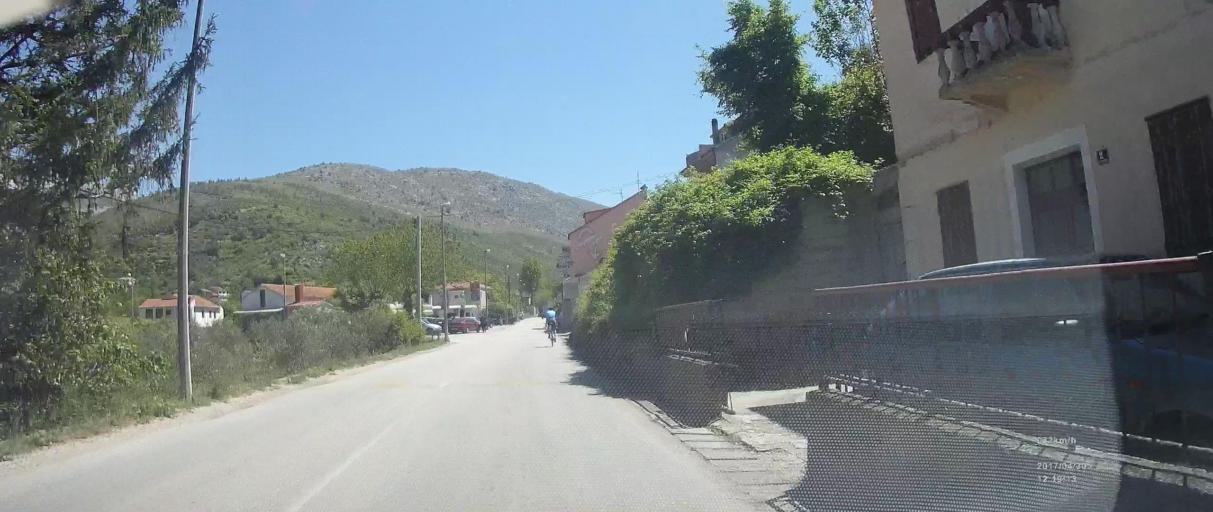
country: HR
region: Splitsko-Dalmatinska
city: Zrnovnica
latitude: 43.5170
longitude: 16.5533
